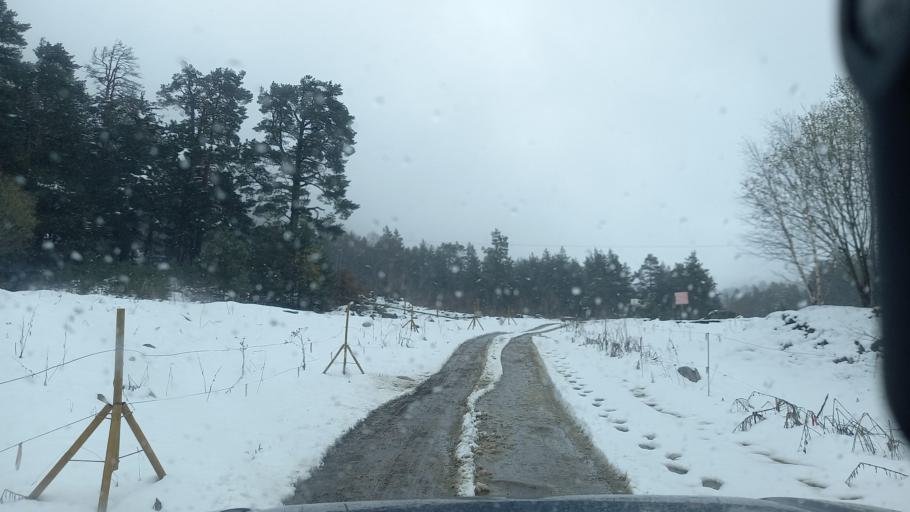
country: RU
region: Kabardino-Balkariya
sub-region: El'brusskiy Rayon
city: El'brus
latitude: 43.2190
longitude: 42.6925
